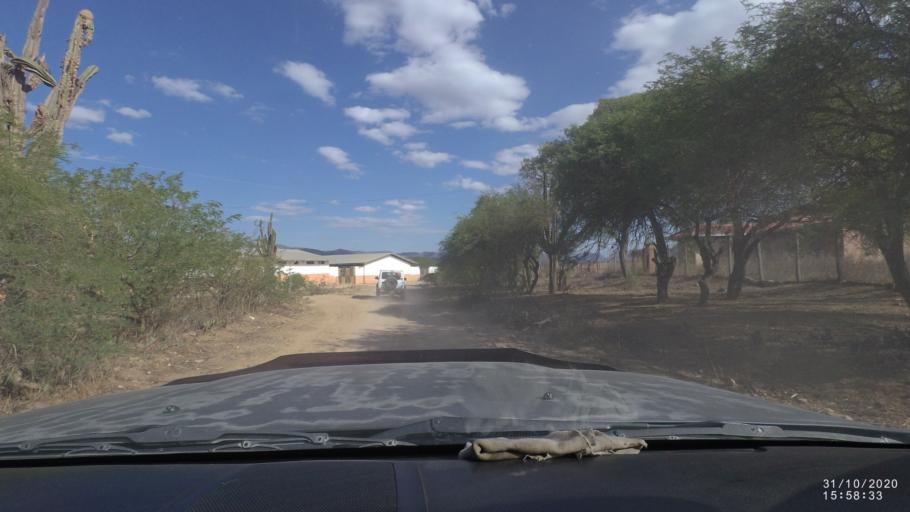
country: BO
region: Chuquisaca
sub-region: Provincia Zudanez
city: Mojocoya
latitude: -18.3258
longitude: -64.6714
